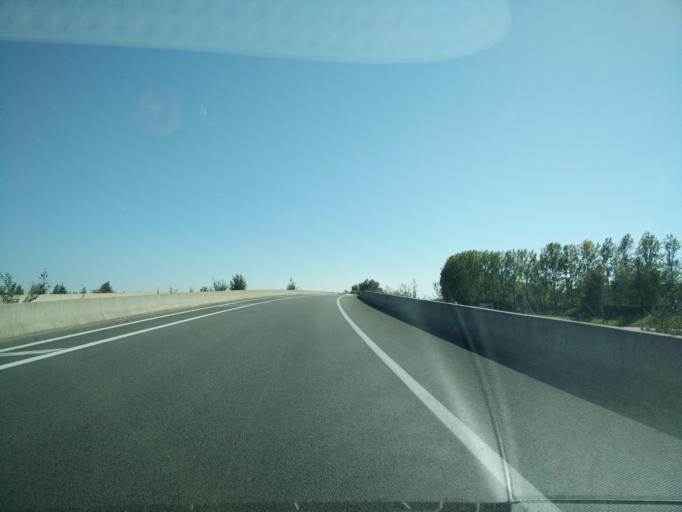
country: FR
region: Ile-de-France
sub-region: Departement de Seine-et-Marne
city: Mitry-Mory
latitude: 48.9932
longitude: 2.6540
